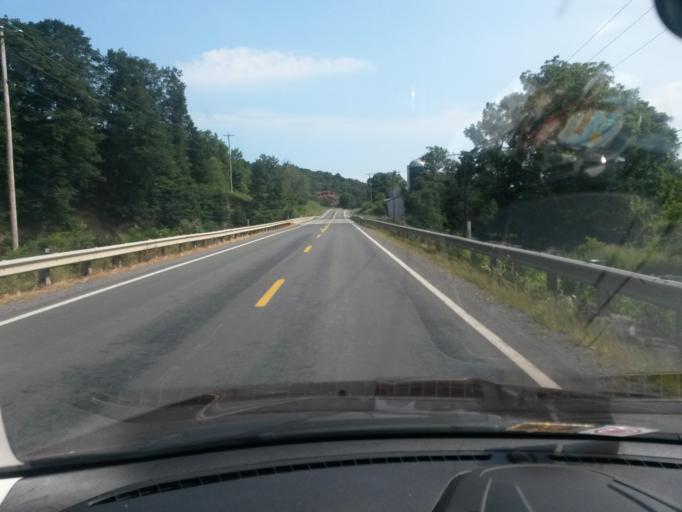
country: US
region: Virginia
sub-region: Shenandoah County
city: Basye
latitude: 38.9616
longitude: -78.8041
